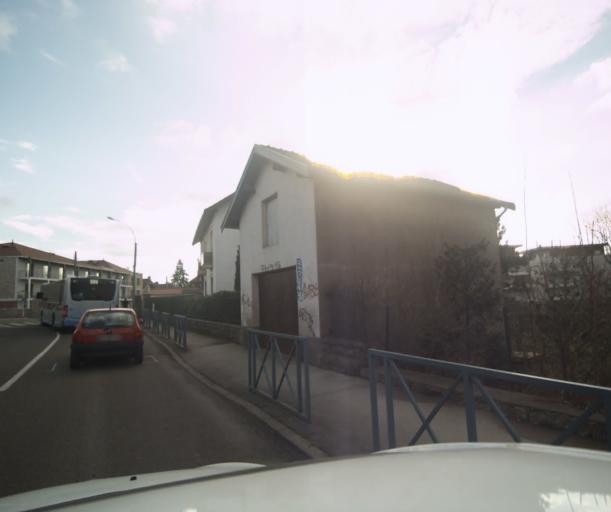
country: FR
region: Franche-Comte
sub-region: Departement du Doubs
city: Besancon
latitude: 47.2537
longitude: 6.0297
